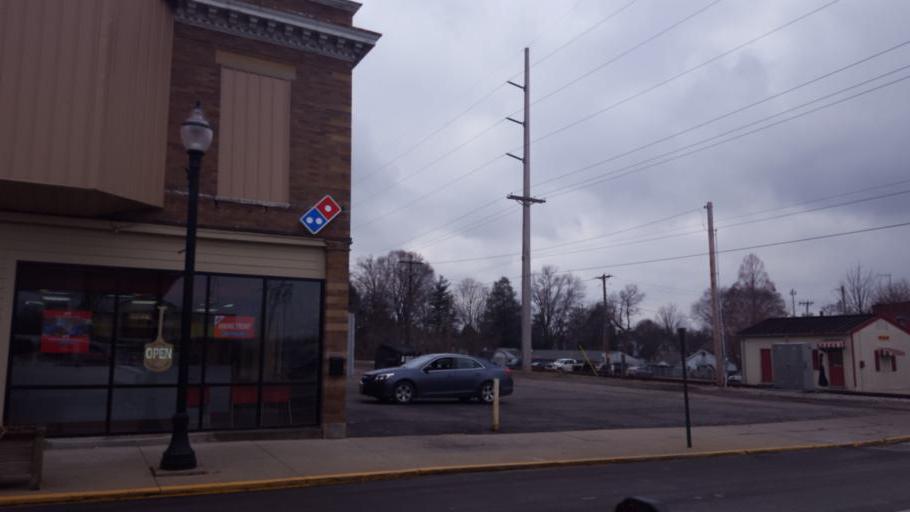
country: US
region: Ohio
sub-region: Richland County
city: Shelby
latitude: 40.8814
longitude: -82.6568
